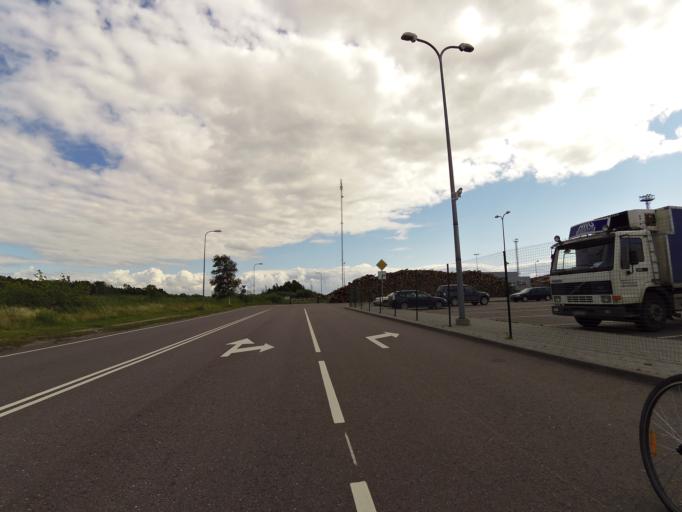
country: EE
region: Laeaene
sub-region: Haapsalu linn
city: Haapsalu
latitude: 58.9056
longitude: 23.4265
